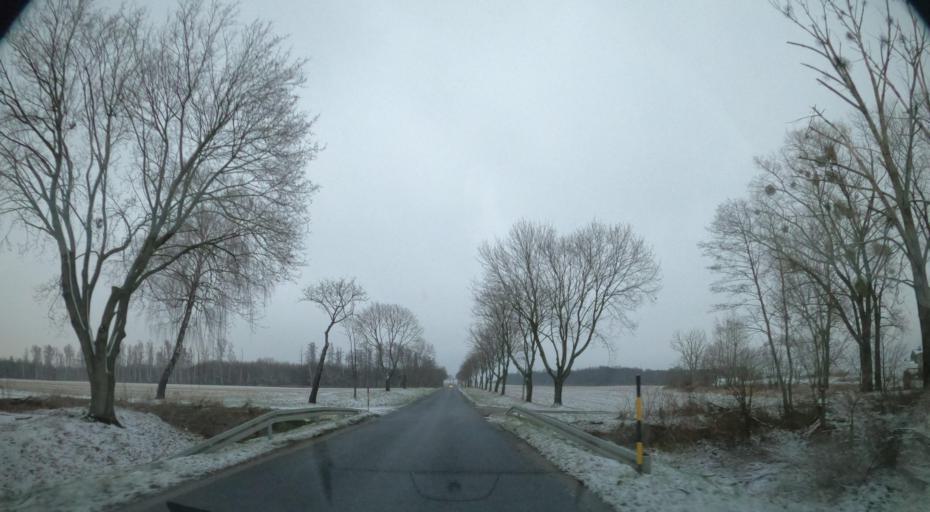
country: PL
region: Kujawsko-Pomorskie
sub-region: Powiat lipnowski
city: Wielgie
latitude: 52.6995
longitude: 19.2837
